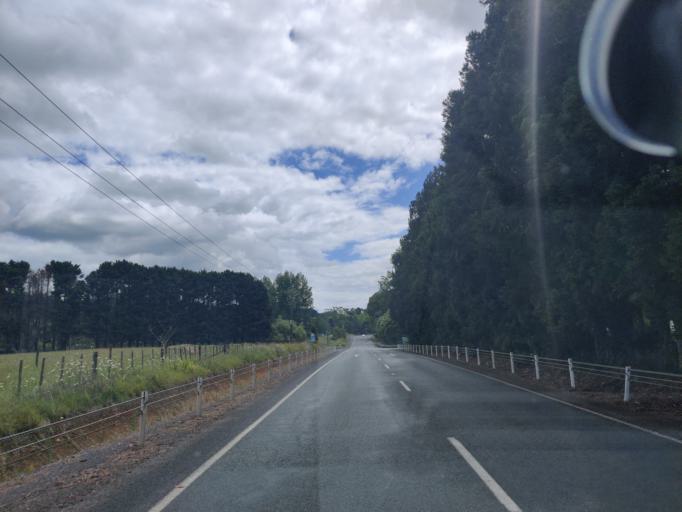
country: NZ
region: Northland
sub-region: Far North District
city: Paihia
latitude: -35.2905
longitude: 174.0198
